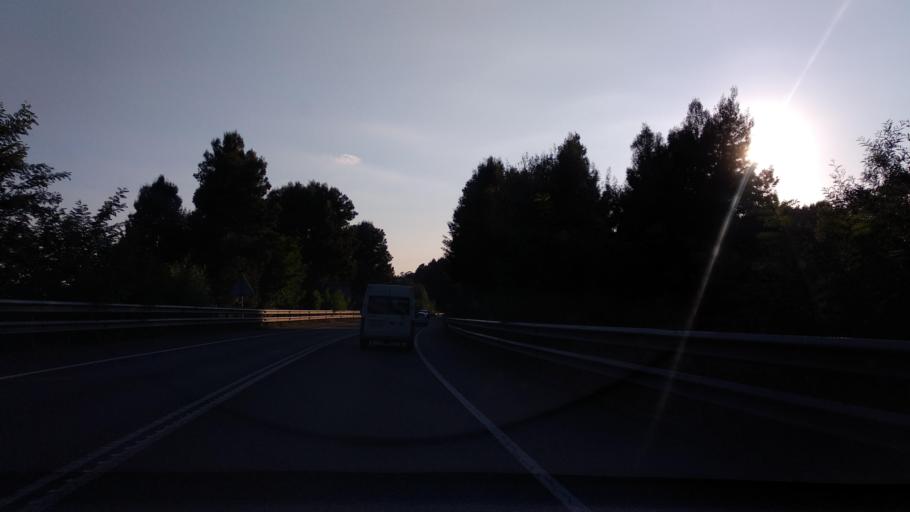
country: ES
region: Galicia
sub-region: Provincia de Pontevedra
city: Moana
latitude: 42.2729
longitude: -8.7591
